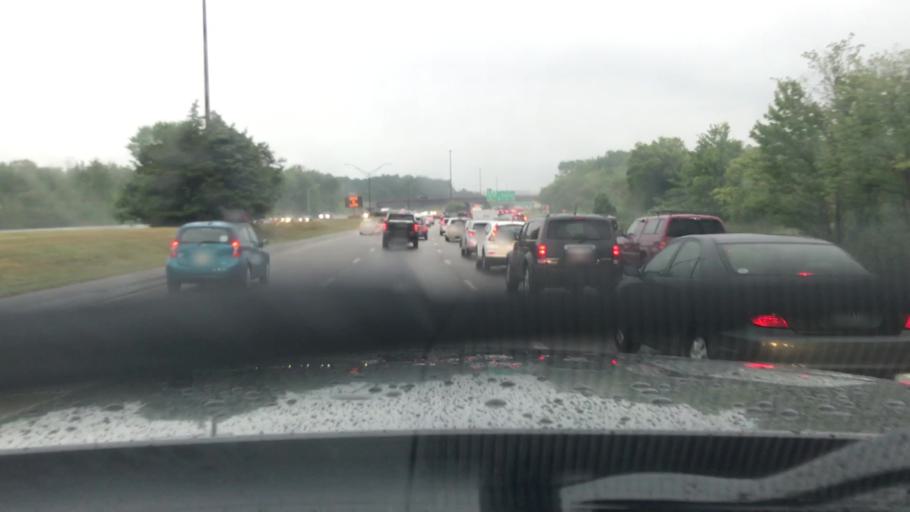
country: US
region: New Hampshire
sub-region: Rockingham County
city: Greenland
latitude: 43.0552
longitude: -70.8078
